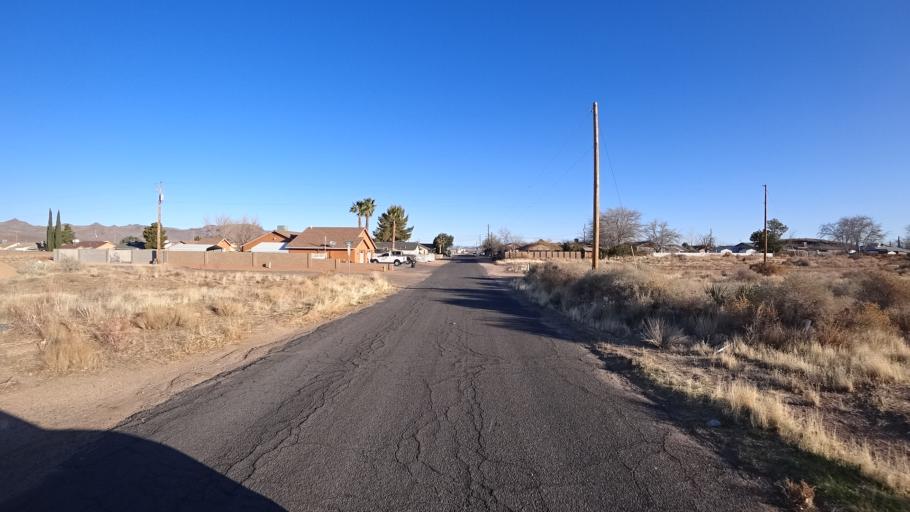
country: US
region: Arizona
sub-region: Mohave County
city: Kingman
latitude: 35.2045
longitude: -114.0137
